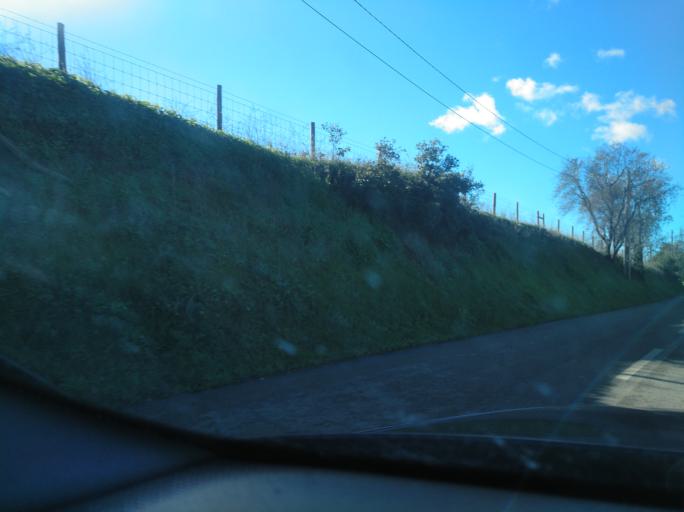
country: PT
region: Faro
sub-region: Vila Real de Santo Antonio
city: Monte Gordo
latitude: 37.1672
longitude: -7.5266
